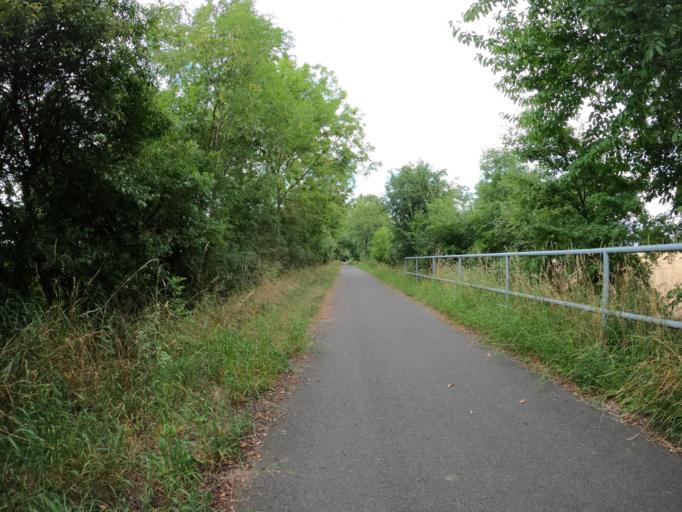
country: DE
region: Mecklenburg-Vorpommern
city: Woldegk
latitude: 53.3740
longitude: 13.5885
